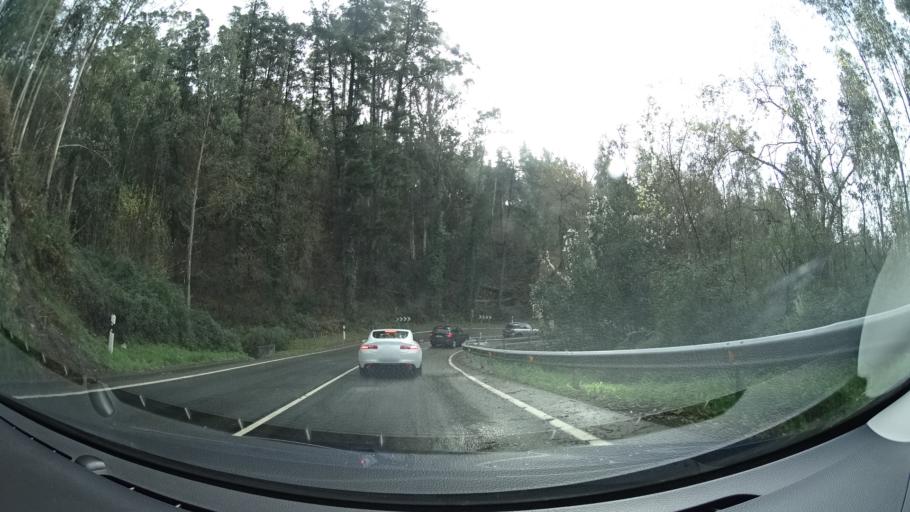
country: ES
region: Basque Country
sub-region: Bizkaia
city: Bakio
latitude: 43.3831
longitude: -2.7887
